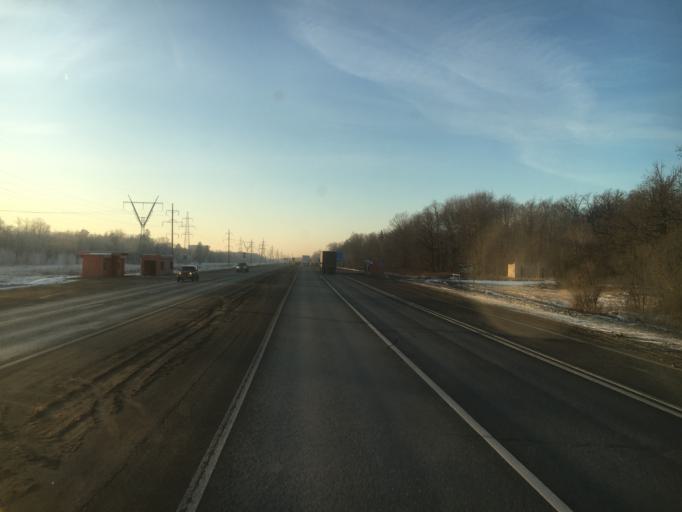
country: RU
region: Samara
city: Pribrezhnyy
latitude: 53.5167
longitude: 49.8522
